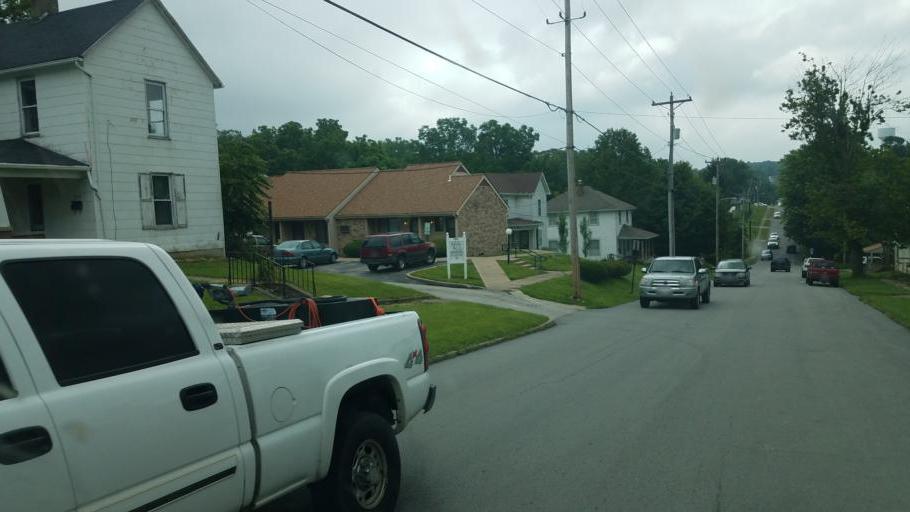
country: US
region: Ohio
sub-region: Highland County
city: Hillsboro
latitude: 39.2001
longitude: -83.6067
